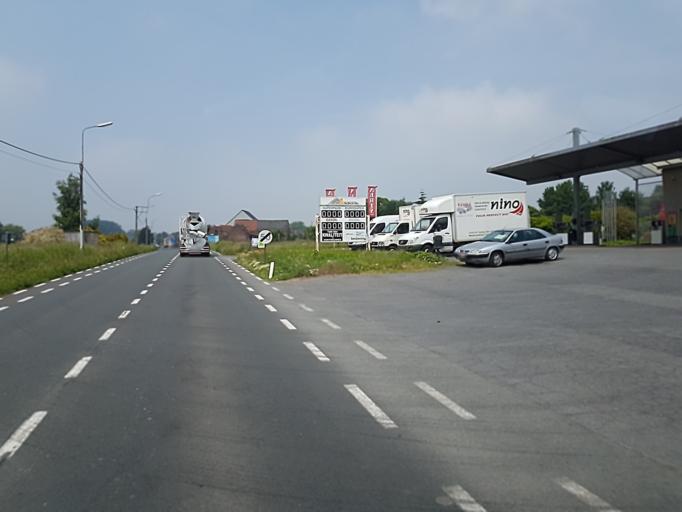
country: BE
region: Flanders
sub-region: Provincie Oost-Vlaanderen
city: Perre
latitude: 50.8613
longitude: 3.8557
